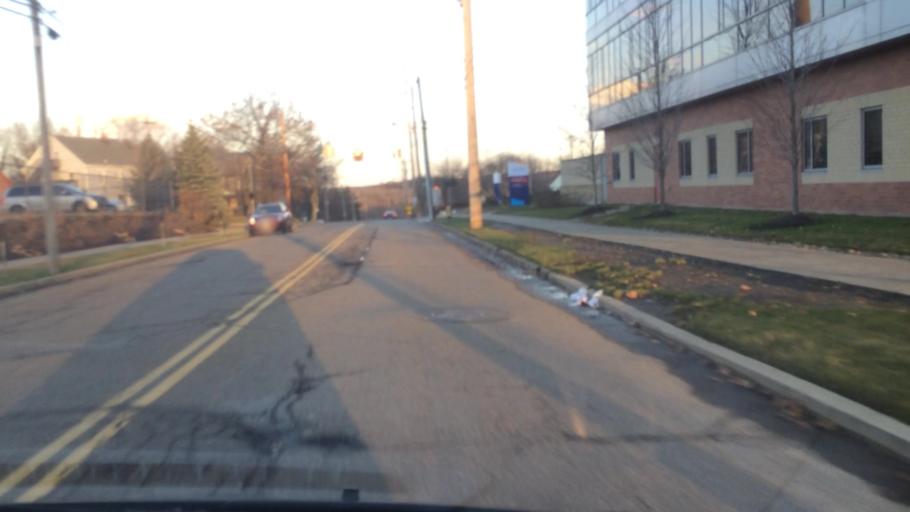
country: US
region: Ohio
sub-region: Summit County
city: Akron
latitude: 41.0824
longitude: -81.5006
